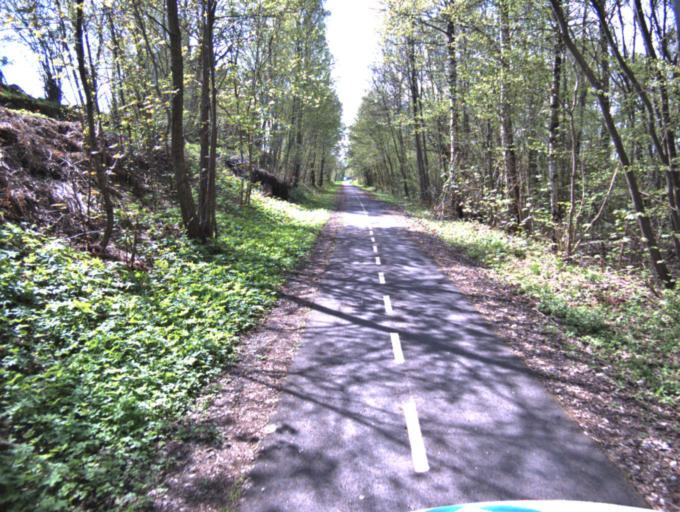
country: SE
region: Skane
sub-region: Kristianstads Kommun
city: Onnestad
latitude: 55.9977
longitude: 14.0399
